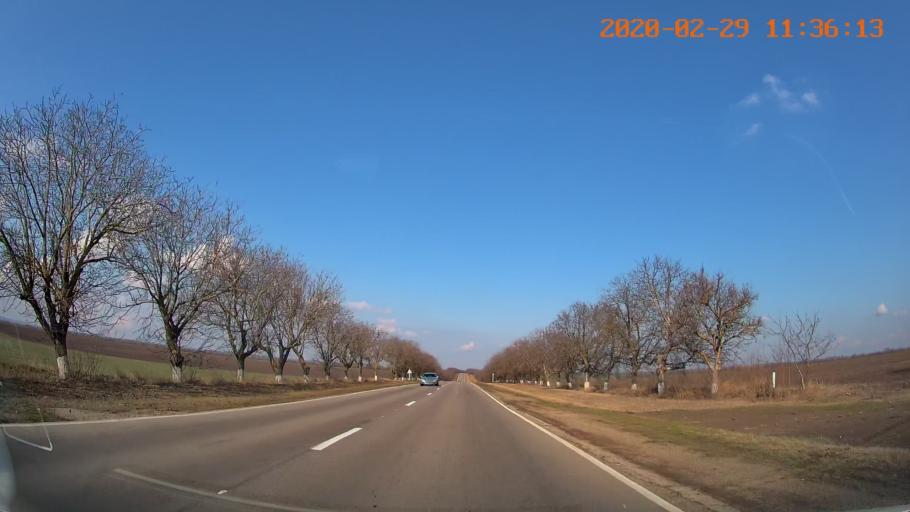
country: MD
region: Rezina
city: Saharna
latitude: 47.5928
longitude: 29.0579
